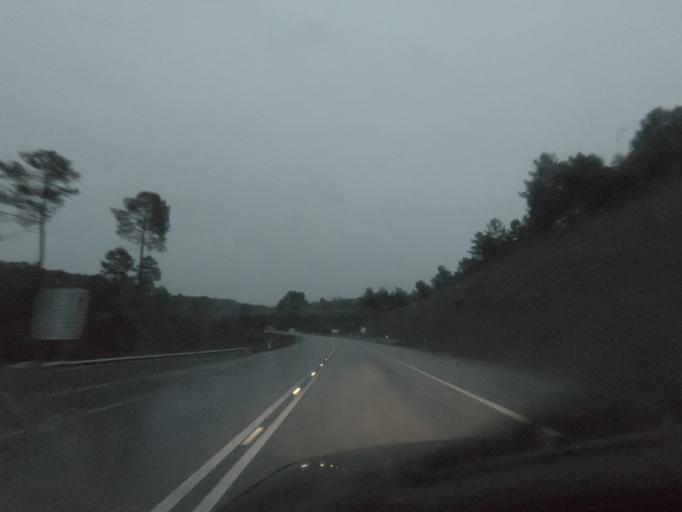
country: PT
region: Vila Real
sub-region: Sabrosa
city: Vilela
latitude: 41.2643
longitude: -7.6725
